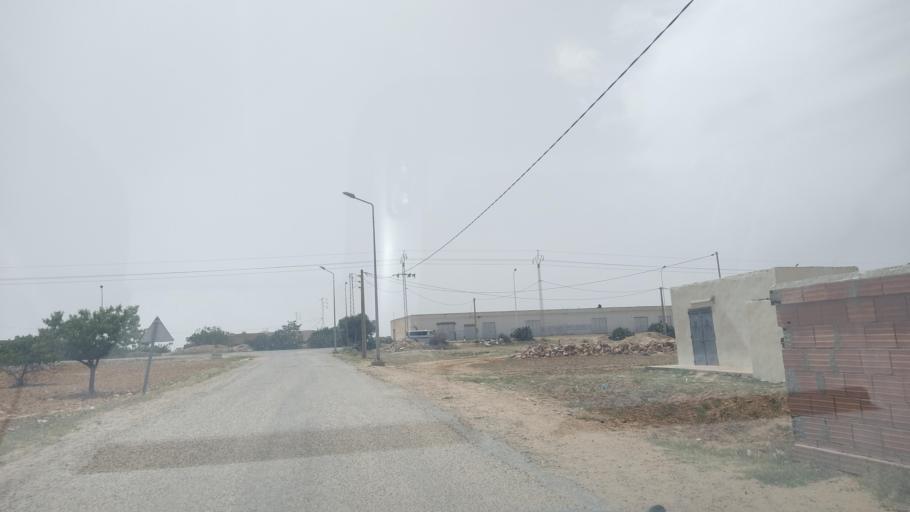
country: TN
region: Safaqis
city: Sfax
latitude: 34.8312
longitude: 10.5987
